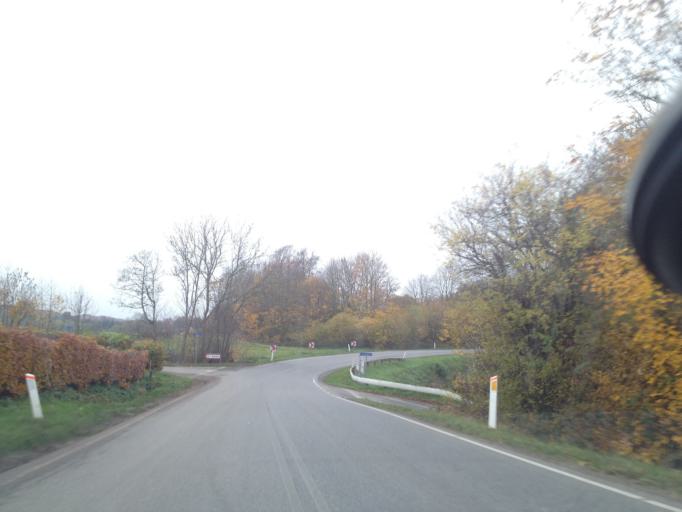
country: DK
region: South Denmark
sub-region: Assens Kommune
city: Vissenbjerg
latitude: 55.4482
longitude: 10.1504
